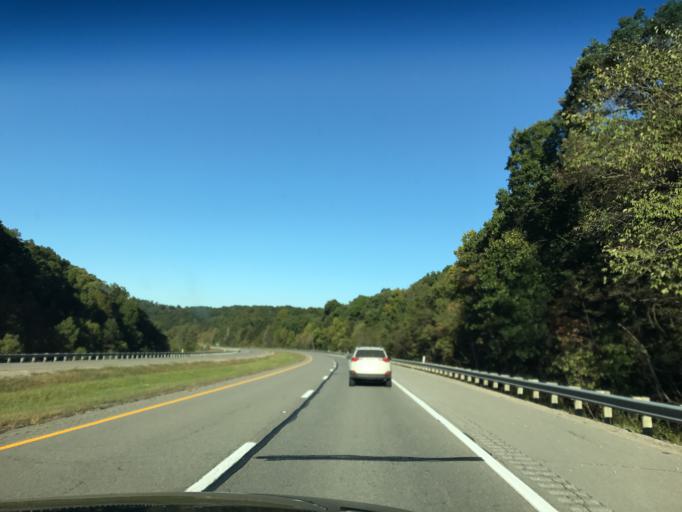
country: US
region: Ohio
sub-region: Washington County
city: Newport
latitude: 39.2583
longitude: -81.2776
